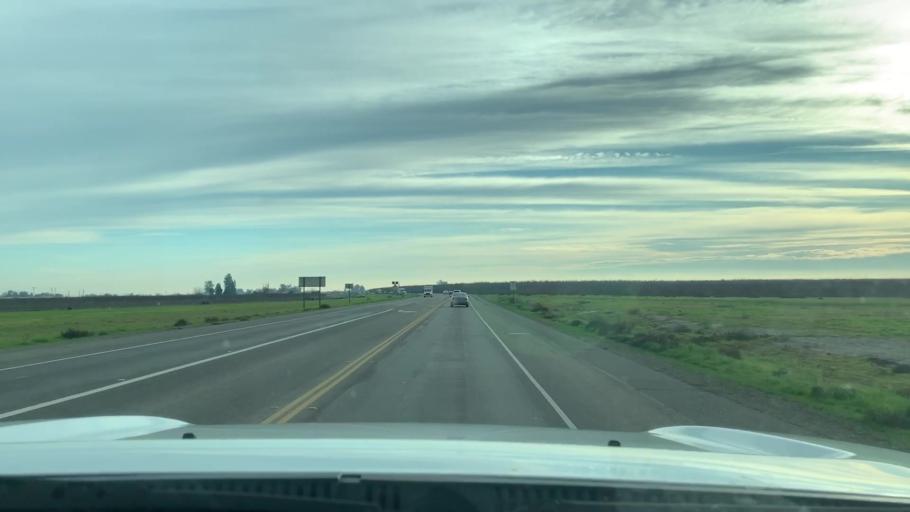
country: US
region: California
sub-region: Fresno County
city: Caruthers
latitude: 36.4879
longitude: -119.7903
